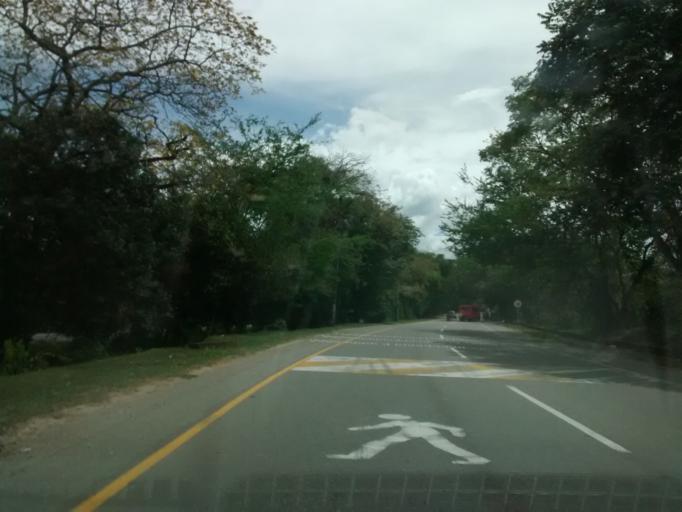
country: CO
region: Tolima
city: Ibague
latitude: 4.4013
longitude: -75.1489
